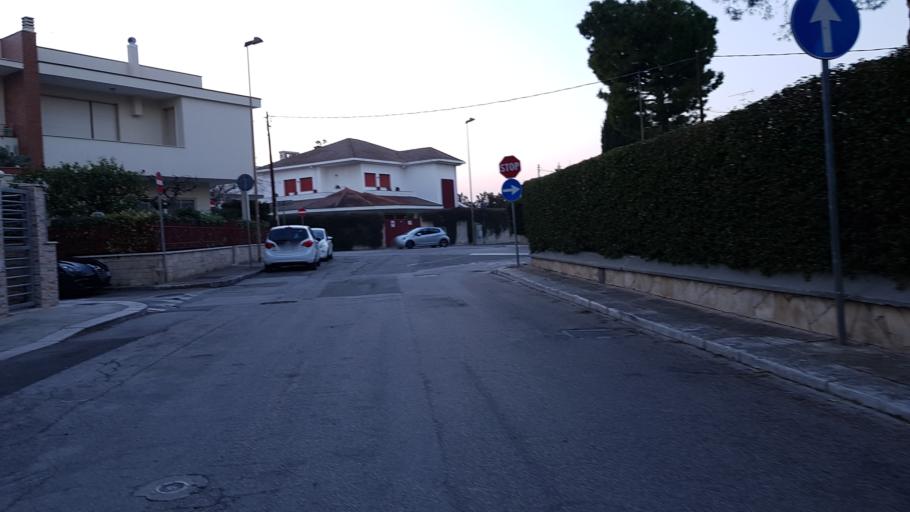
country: IT
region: Apulia
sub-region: Provincia di Brindisi
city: Brindisi
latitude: 40.6462
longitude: 17.9371
